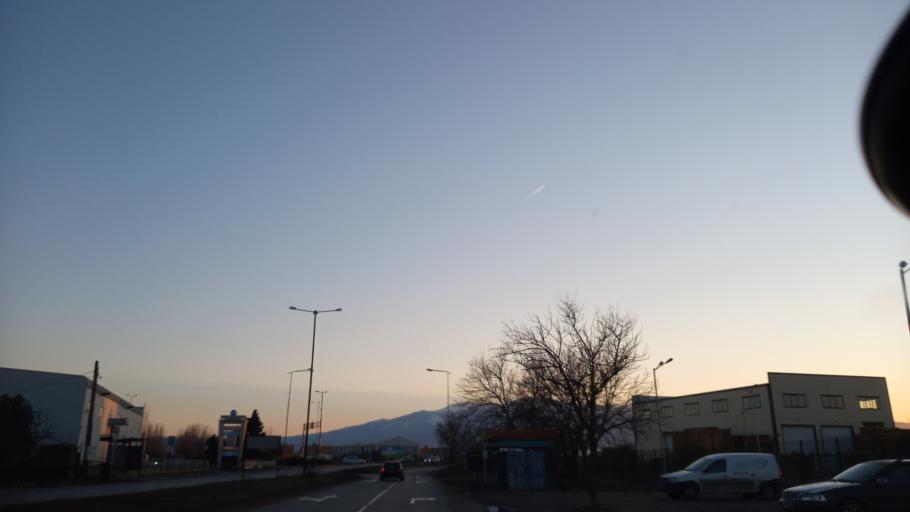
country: BG
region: Sofia-Capital
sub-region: Stolichna Obshtina
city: Sofia
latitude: 42.7103
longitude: 23.4318
